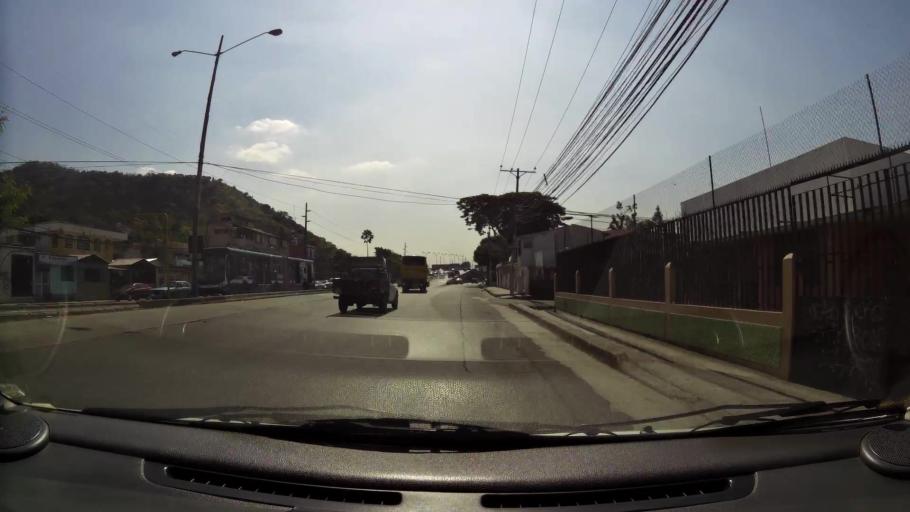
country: EC
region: Guayas
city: Guayaquil
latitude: -2.1689
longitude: -79.9196
